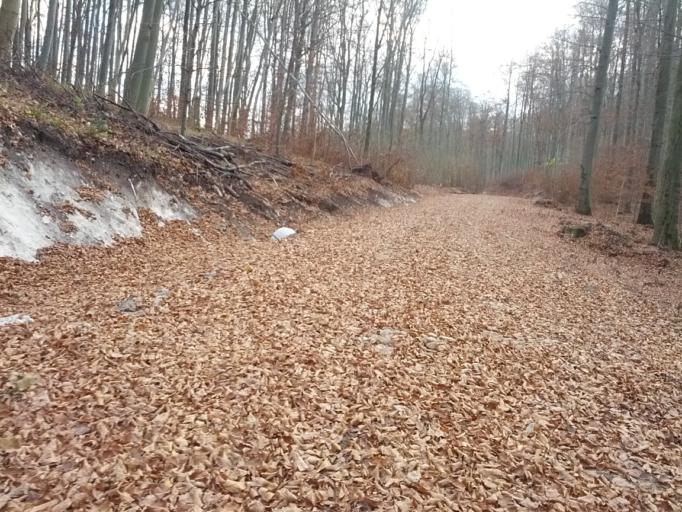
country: DE
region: Thuringia
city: Krauthausen
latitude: 50.9771
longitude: 10.2341
